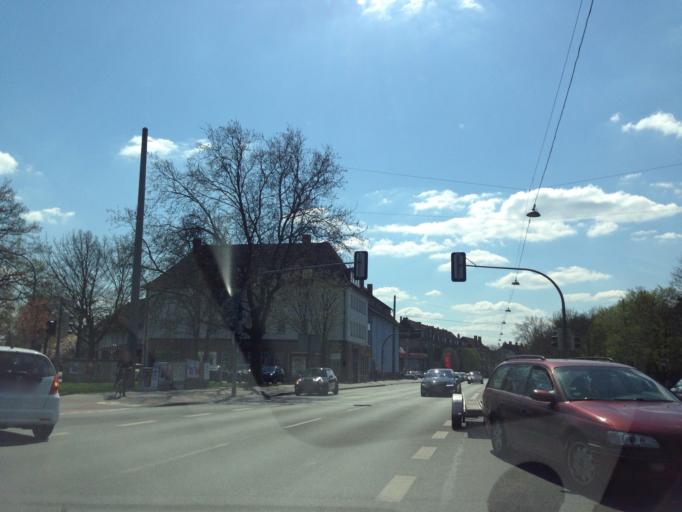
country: DE
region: North Rhine-Westphalia
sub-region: Regierungsbezirk Munster
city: Muenster
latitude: 51.9410
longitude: 7.6094
